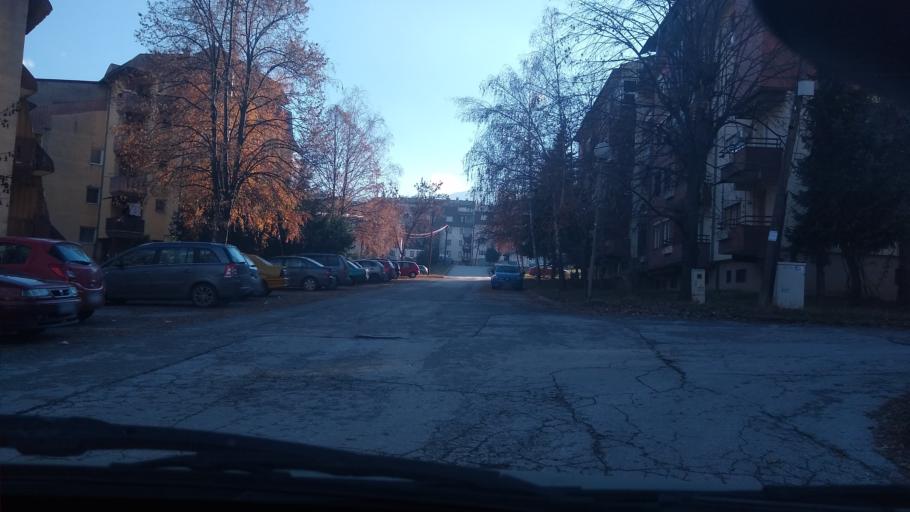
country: MK
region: Bitola
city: Bitola
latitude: 41.0239
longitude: 21.3149
